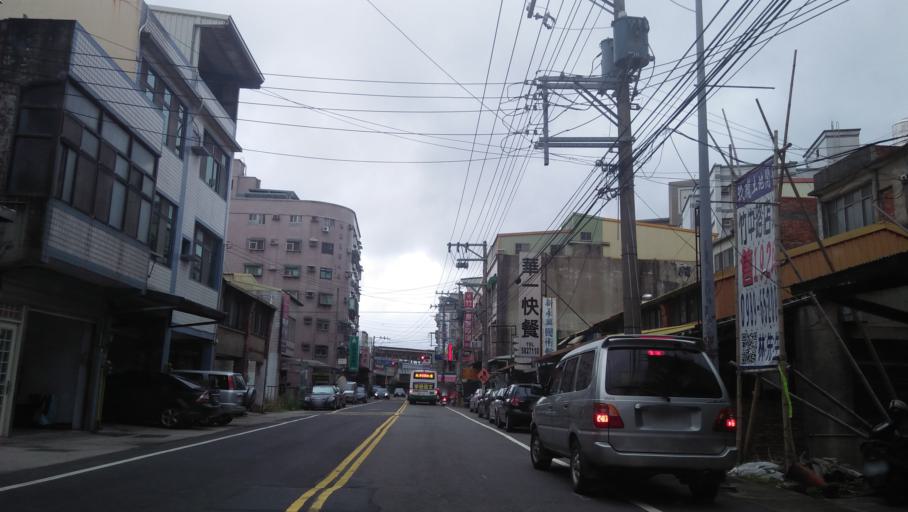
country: TW
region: Taiwan
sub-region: Hsinchu
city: Zhubei
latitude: 24.7810
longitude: 121.0290
